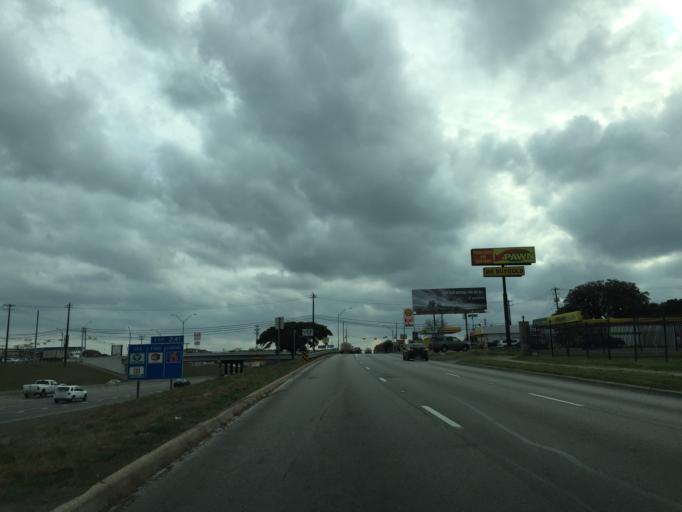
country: US
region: Texas
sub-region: Travis County
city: Wells Branch
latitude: 30.3787
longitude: -97.6755
